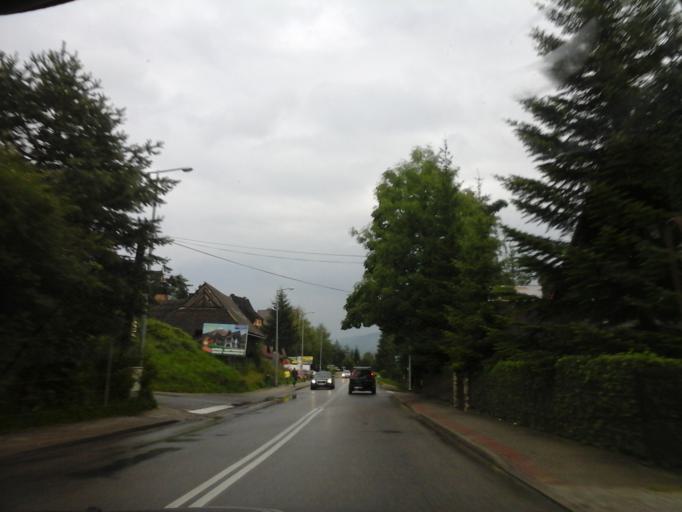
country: PL
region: Lesser Poland Voivodeship
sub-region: Powiat tatrzanski
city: Koscielisko
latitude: 49.2912
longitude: 19.9130
